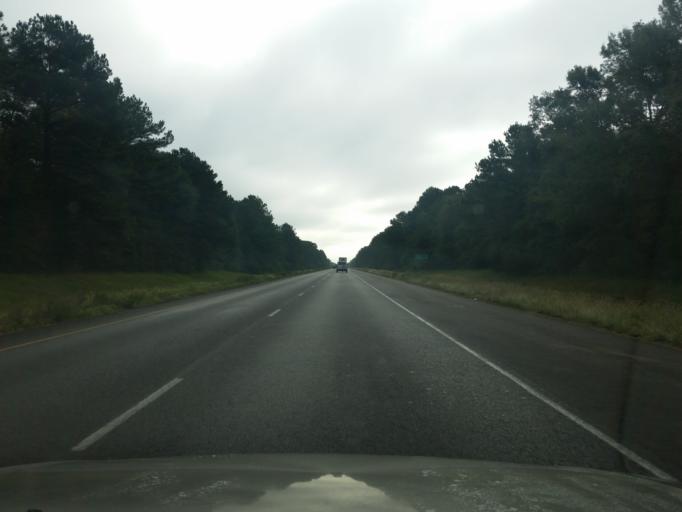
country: US
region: Alabama
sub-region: Baldwin County
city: Spanish Fort
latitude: 30.6618
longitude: -87.8382
